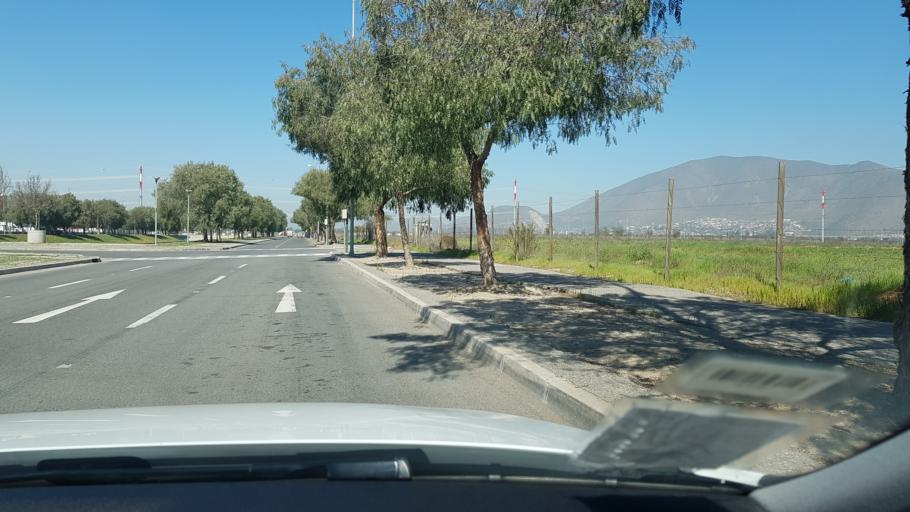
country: CL
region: Santiago Metropolitan
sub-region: Provincia de Santiago
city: Lo Prado
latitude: -33.4283
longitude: -70.8006
